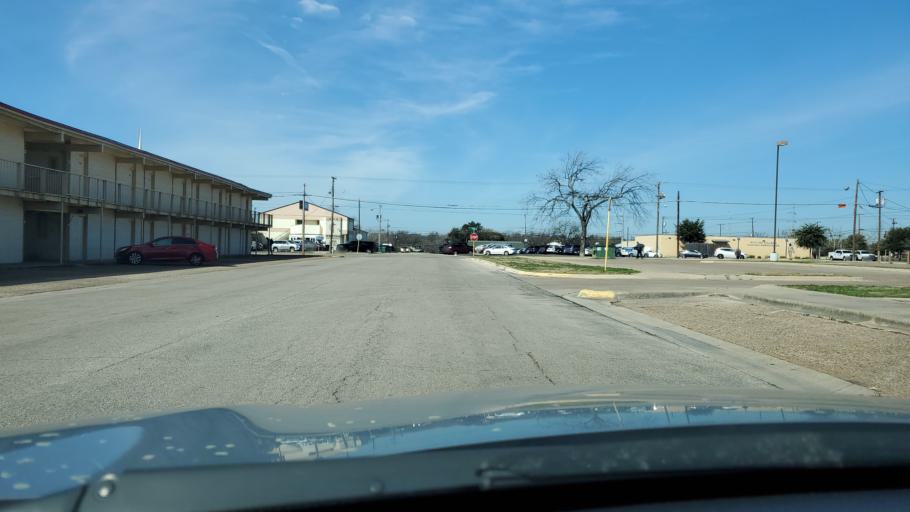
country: US
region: Texas
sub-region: Bell County
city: Killeen
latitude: 31.1237
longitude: -97.7271
